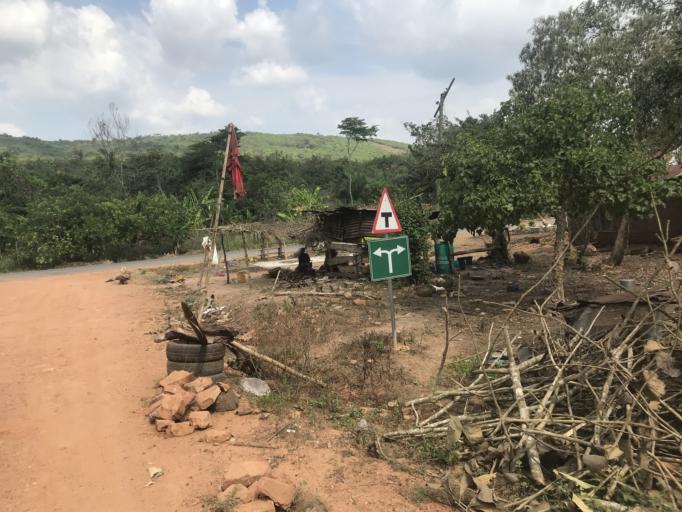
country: NG
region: Osun
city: Inisa
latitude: 7.8963
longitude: 4.3999
